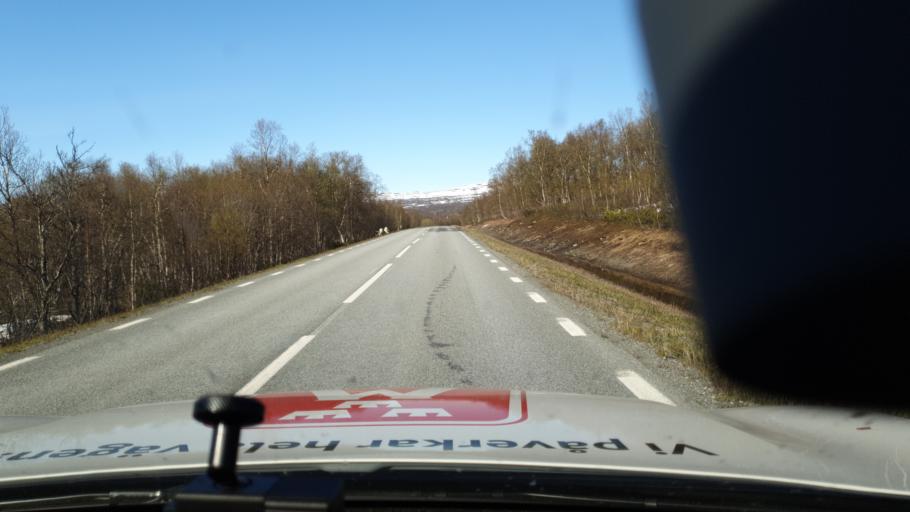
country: NO
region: Nordland
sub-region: Rana
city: Mo i Rana
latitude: 65.9945
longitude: 15.0778
